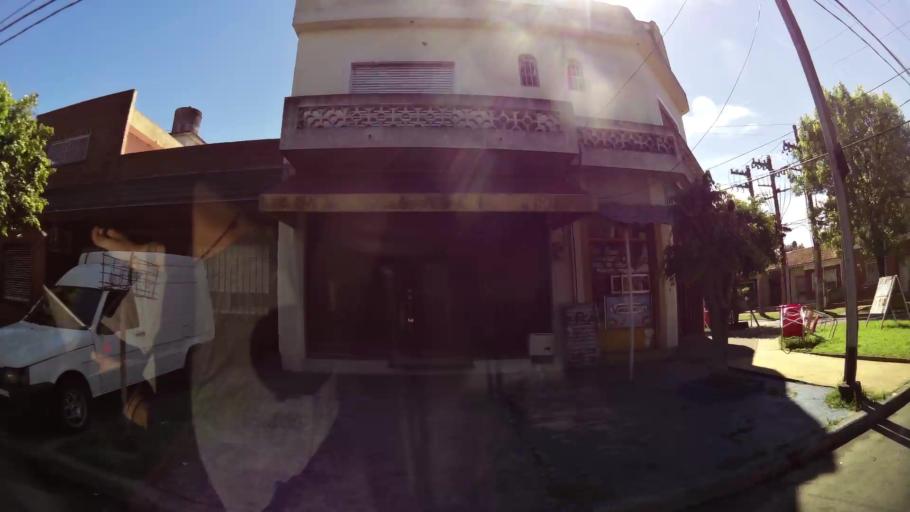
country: AR
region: Buenos Aires
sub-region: Partido de Quilmes
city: Quilmes
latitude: -34.6939
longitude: -58.3039
